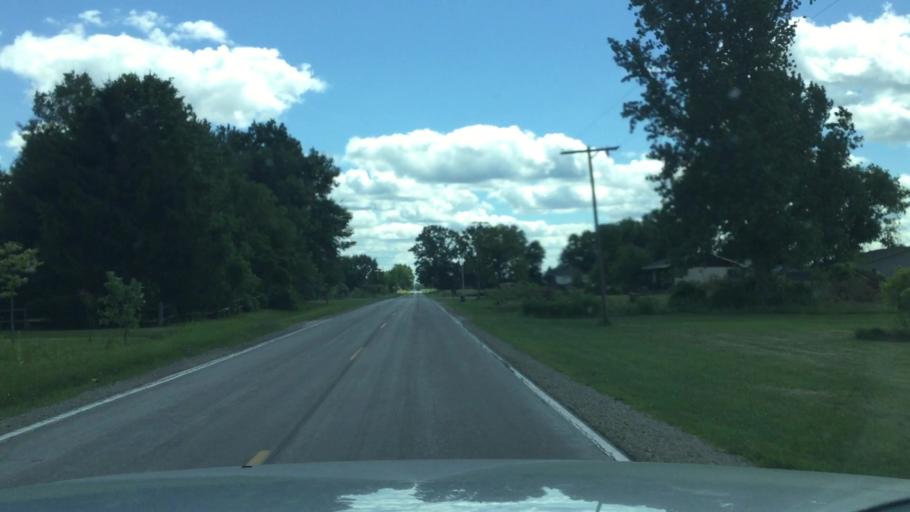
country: US
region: Michigan
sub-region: Saginaw County
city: Saint Charles
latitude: 43.3503
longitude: -84.1900
